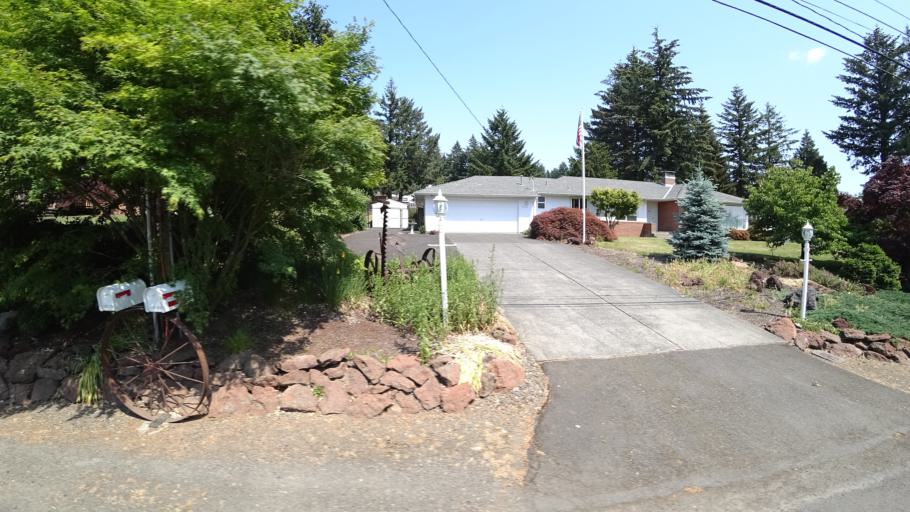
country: US
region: Oregon
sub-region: Multnomah County
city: Lents
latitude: 45.4496
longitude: -122.5677
